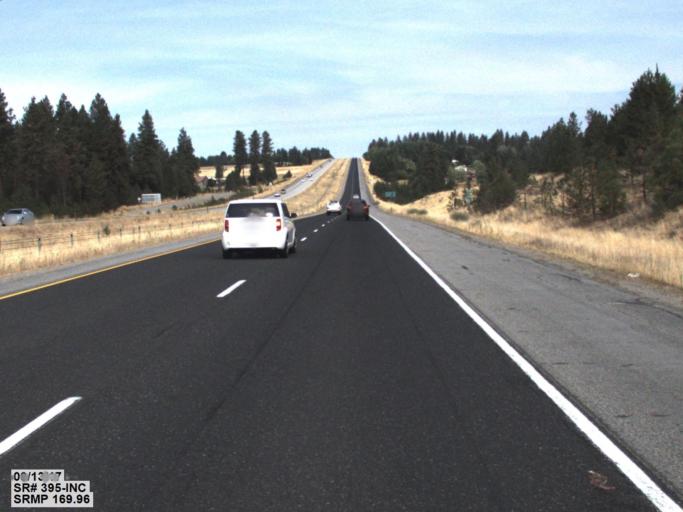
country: US
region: Washington
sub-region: Spokane County
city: Fairwood
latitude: 47.8163
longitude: -117.4099
